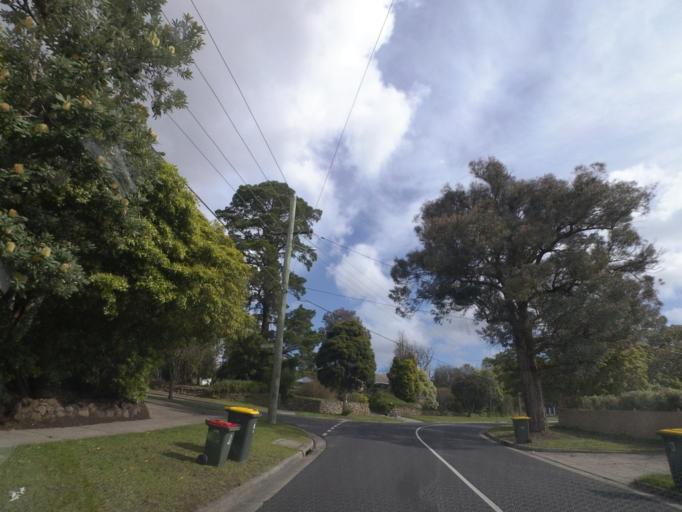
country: AU
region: Victoria
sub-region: Whitehorse
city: Vermont
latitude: -37.8401
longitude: 145.2055
